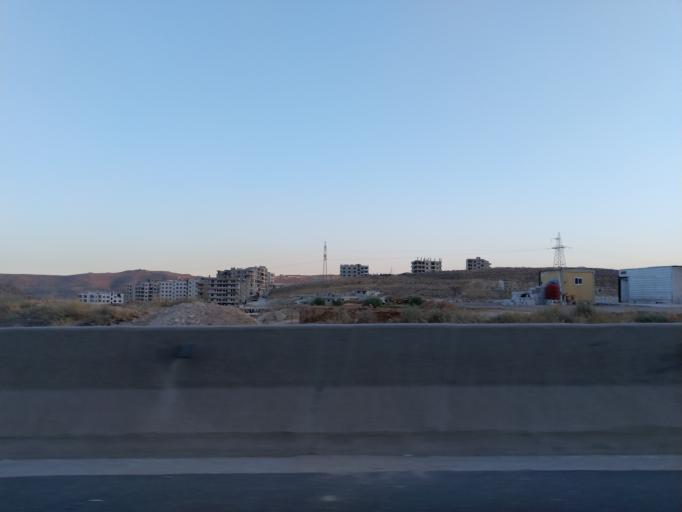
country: SY
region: Rif-dimashq
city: At Tall
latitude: 33.5860
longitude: 36.2984
